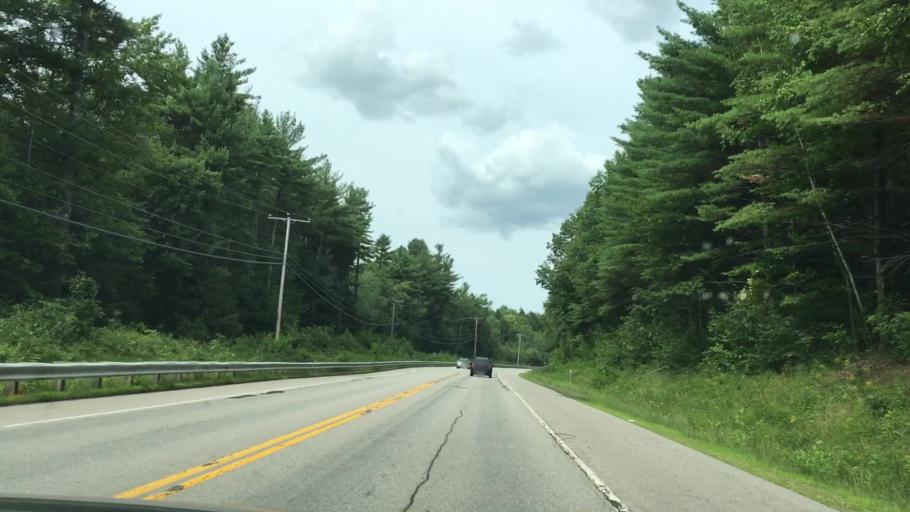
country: US
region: New Hampshire
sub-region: Cheshire County
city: Jaffrey
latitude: 42.8305
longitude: -71.9929
